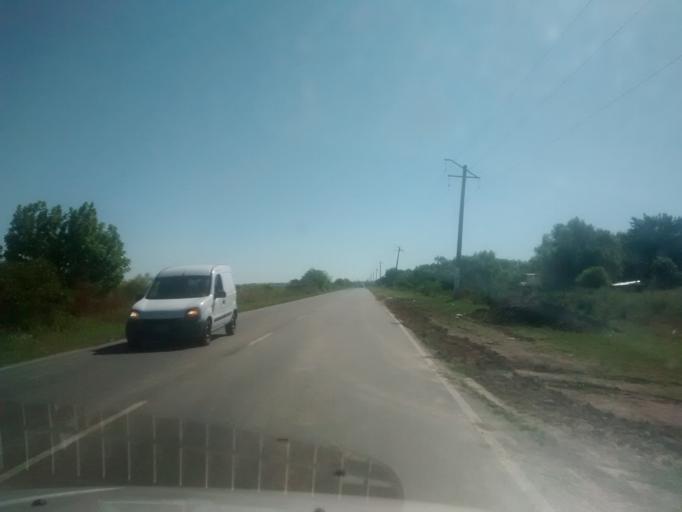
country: AR
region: Buenos Aires
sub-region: Partido de Berisso
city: Berisso
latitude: -34.8873
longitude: -57.8628
